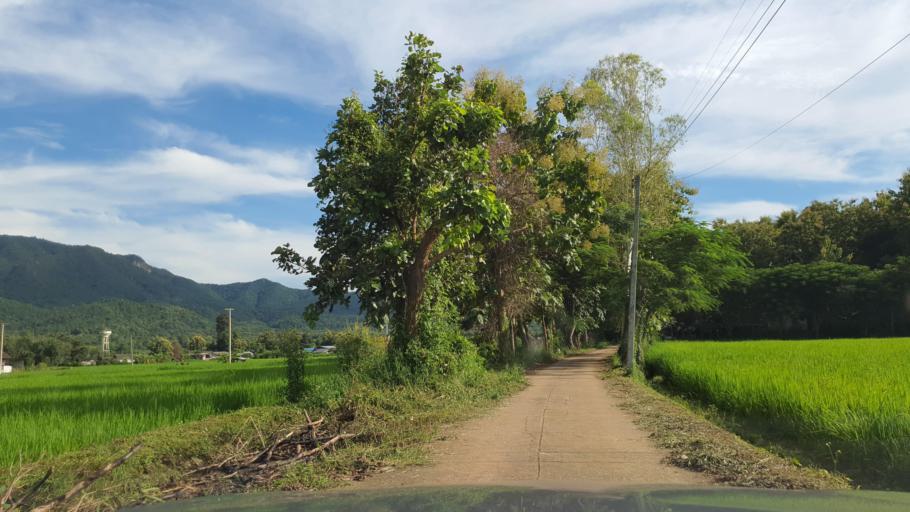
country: TH
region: Chiang Mai
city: Mae On
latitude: 18.7637
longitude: 99.2554
